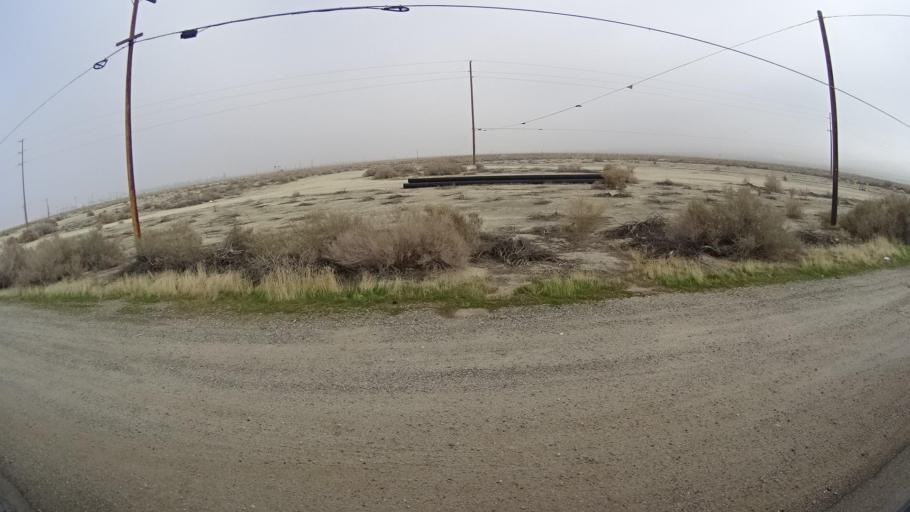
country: US
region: California
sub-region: Kern County
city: Ford City
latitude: 35.1927
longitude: -119.4289
